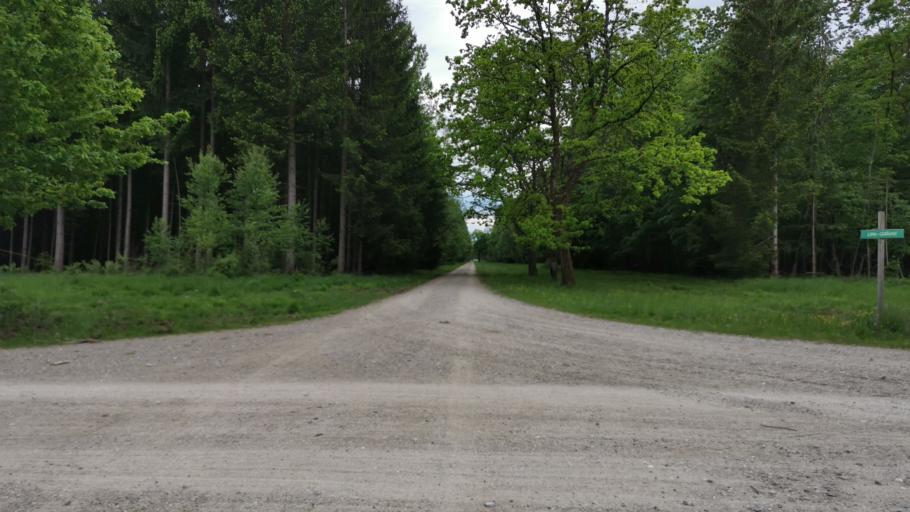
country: DE
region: Bavaria
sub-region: Upper Bavaria
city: Pullach im Isartal
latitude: 48.0617
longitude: 11.4991
